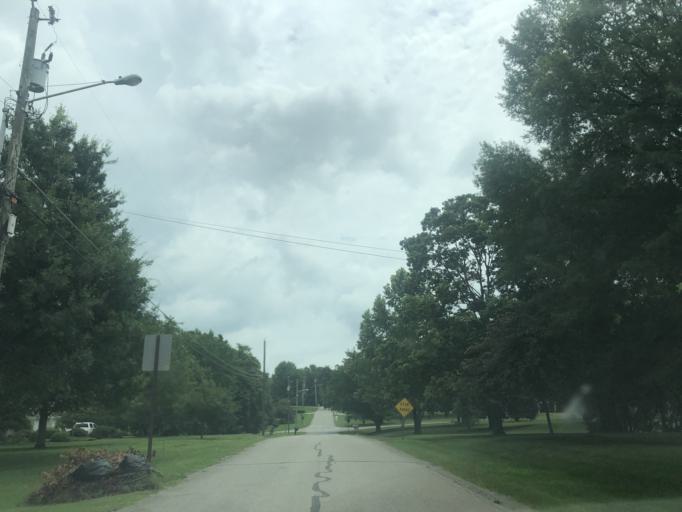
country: US
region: Tennessee
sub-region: Davidson County
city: Oak Hill
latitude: 36.0850
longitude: -86.7860
